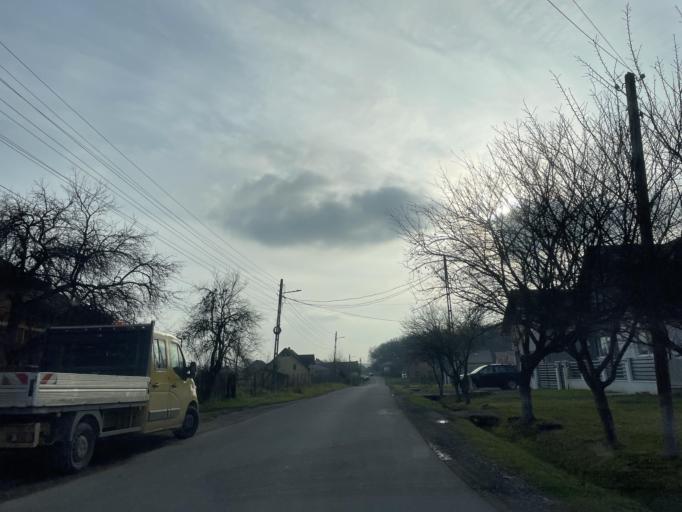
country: RO
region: Mures
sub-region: Comuna Solovastru
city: Solovastru
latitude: 46.7751
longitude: 24.7617
